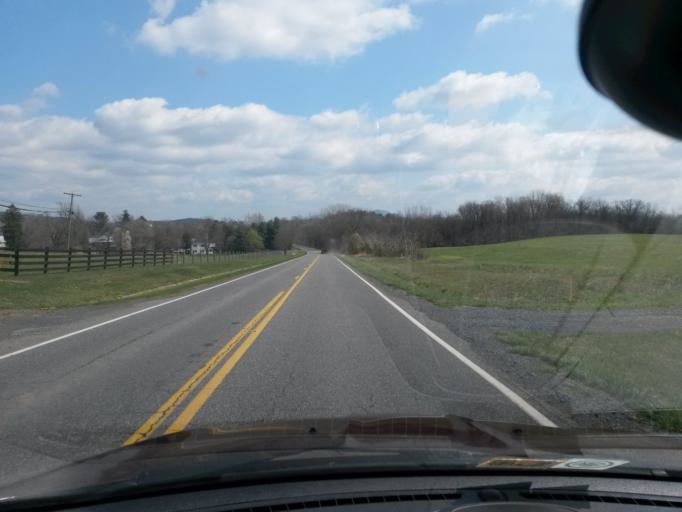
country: US
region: Virginia
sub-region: Augusta County
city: Weyers Cave
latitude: 38.3022
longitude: -78.8972
